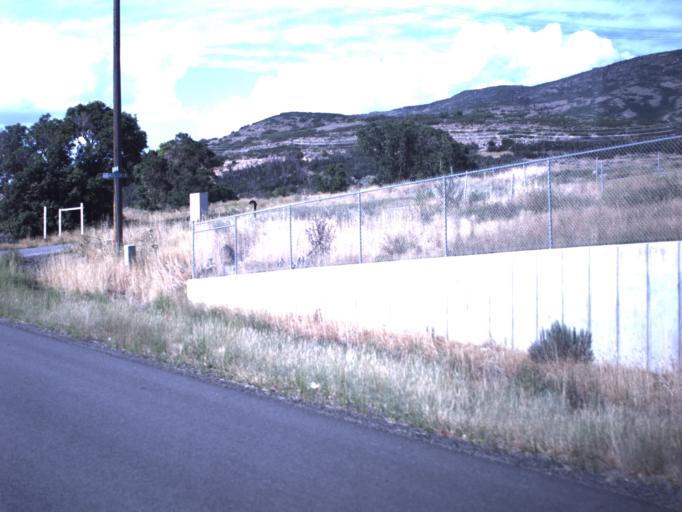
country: US
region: Utah
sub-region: Wasatch County
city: Heber
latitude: 40.5510
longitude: -111.4220
